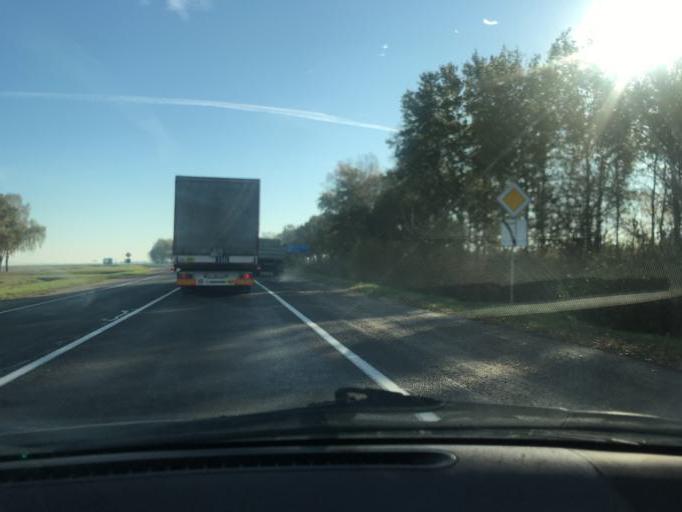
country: BY
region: Brest
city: Ivanava
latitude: 52.1461
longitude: 25.4628
